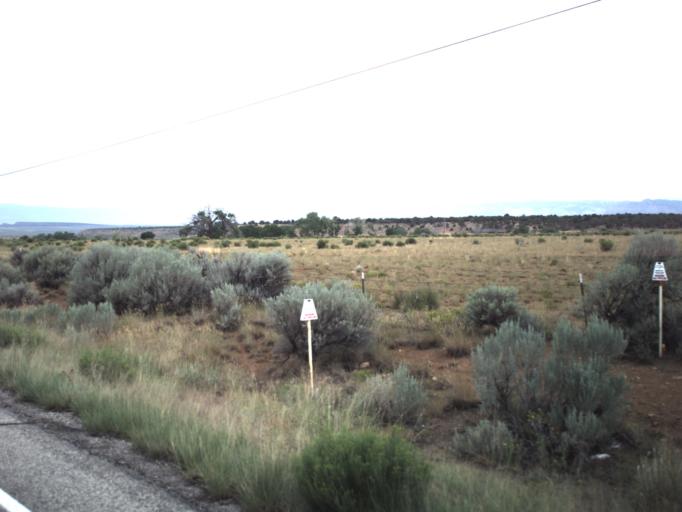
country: US
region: Utah
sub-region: Carbon County
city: East Carbon City
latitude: 39.5364
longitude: -110.4600
